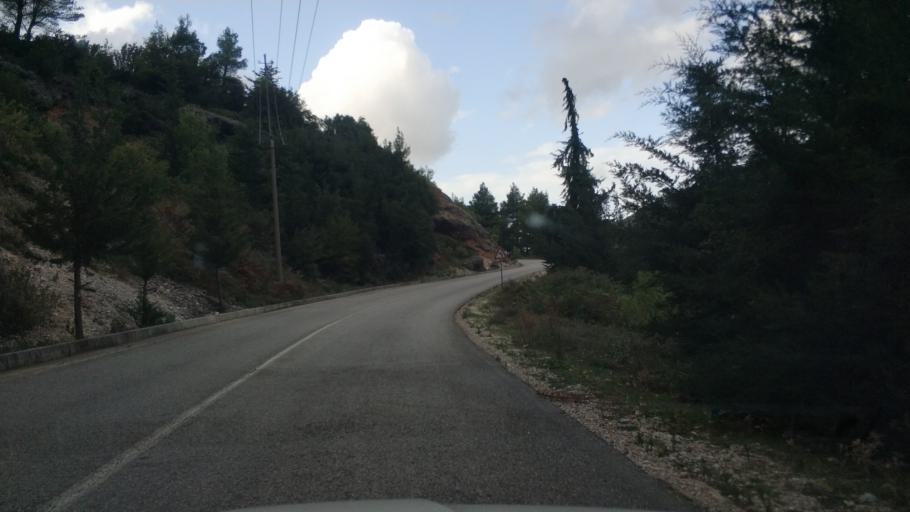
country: AL
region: Vlore
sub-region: Rrethi i Vlores
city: Orikum
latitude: 40.2499
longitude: 19.5424
